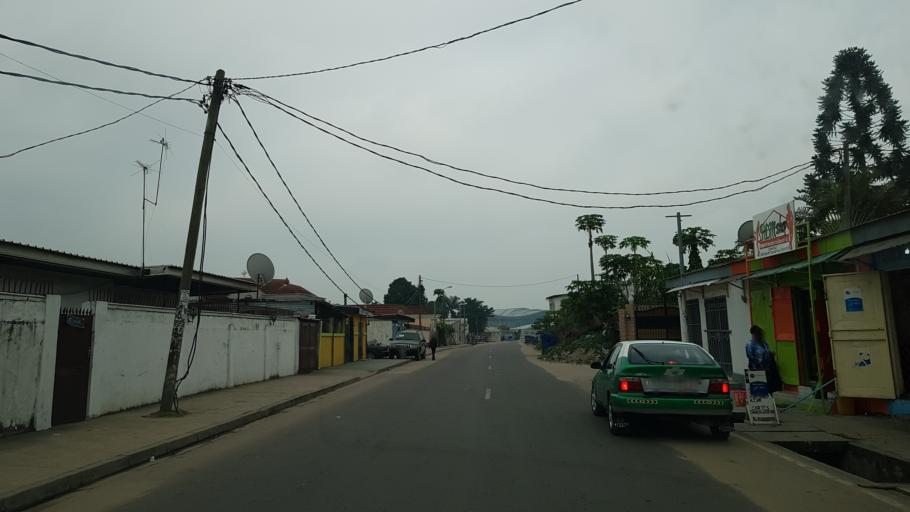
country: CG
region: Brazzaville
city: Brazzaville
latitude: -4.2582
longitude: 15.2582
